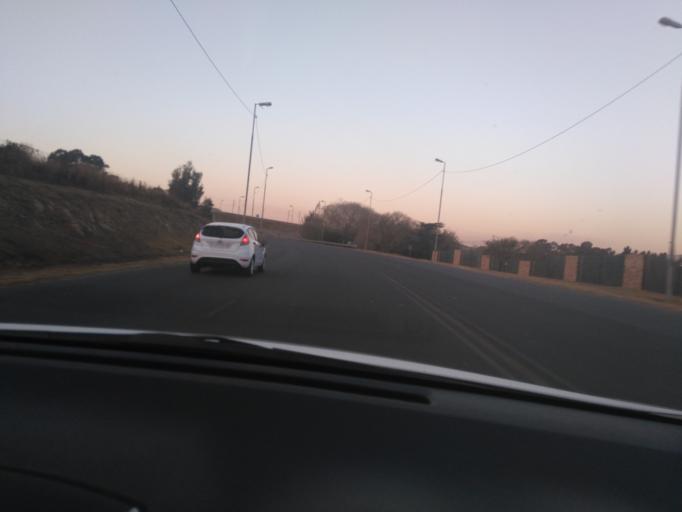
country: ZA
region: Gauteng
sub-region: City of Johannesburg Metropolitan Municipality
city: Modderfontein
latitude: -26.1026
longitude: 28.1692
